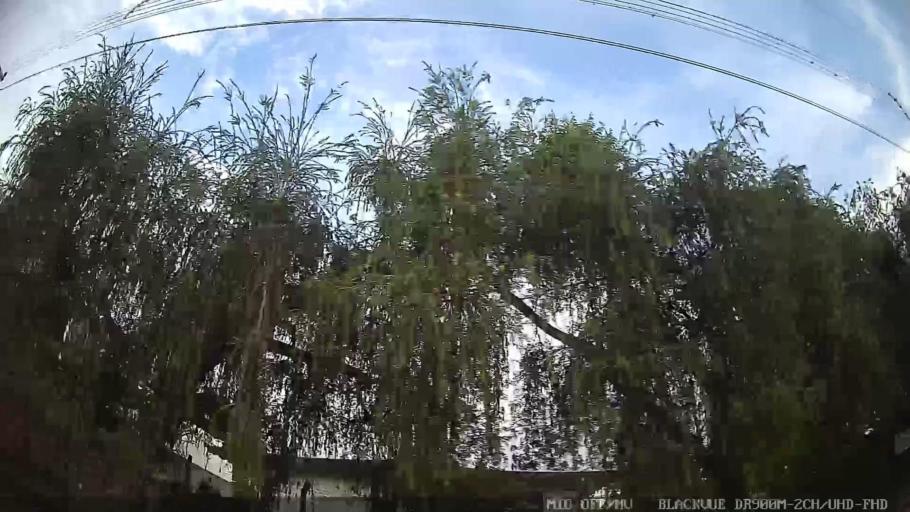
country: BR
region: Sao Paulo
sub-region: Braganca Paulista
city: Braganca Paulista
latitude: -22.9400
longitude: -46.5371
